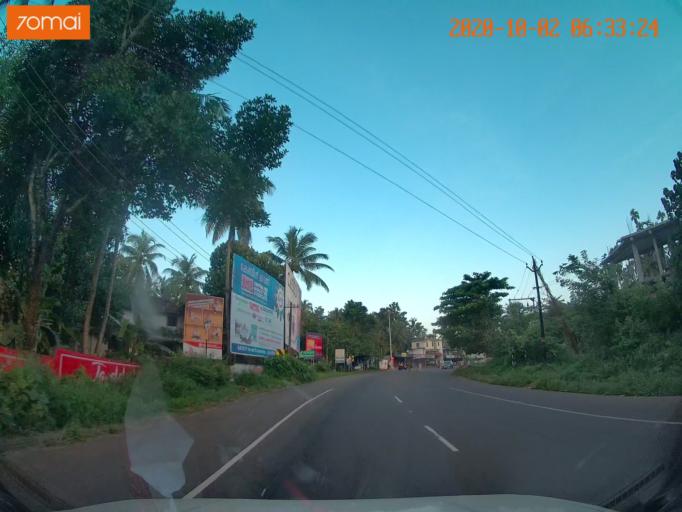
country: IN
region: Kerala
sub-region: Malappuram
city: Ponnani
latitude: 10.7595
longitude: 76.0155
